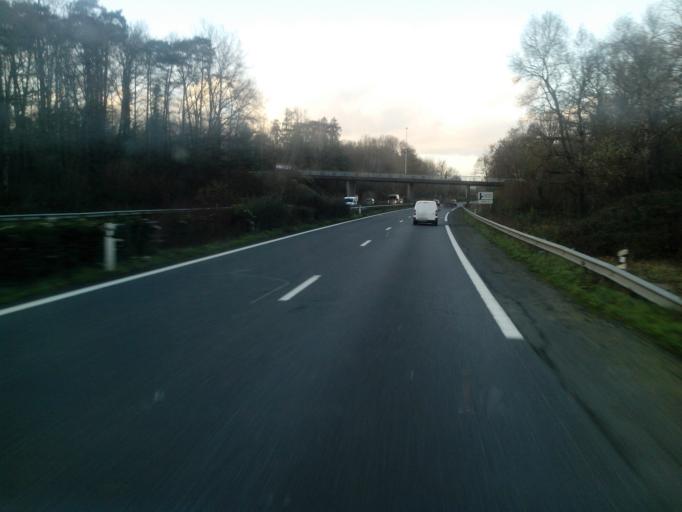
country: FR
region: Pays de la Loire
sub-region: Departement de la Loire-Atlantique
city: Haute-Goulaine
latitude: 47.1995
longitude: -1.4479
